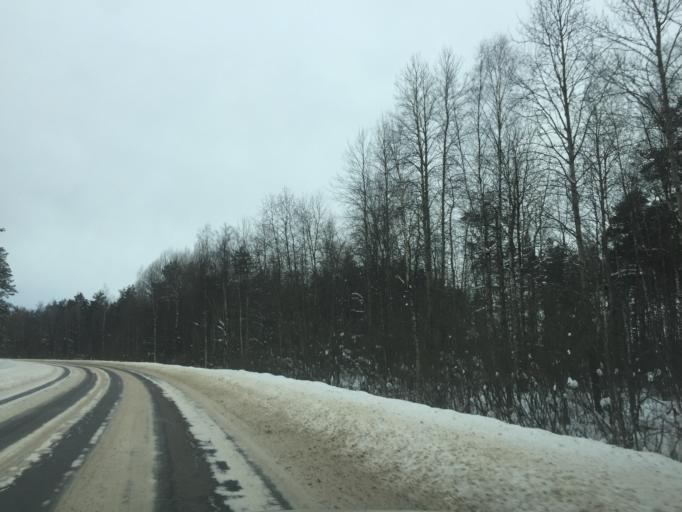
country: RU
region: Leningrad
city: Imeni Sverdlova
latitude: 59.8498
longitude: 30.6597
